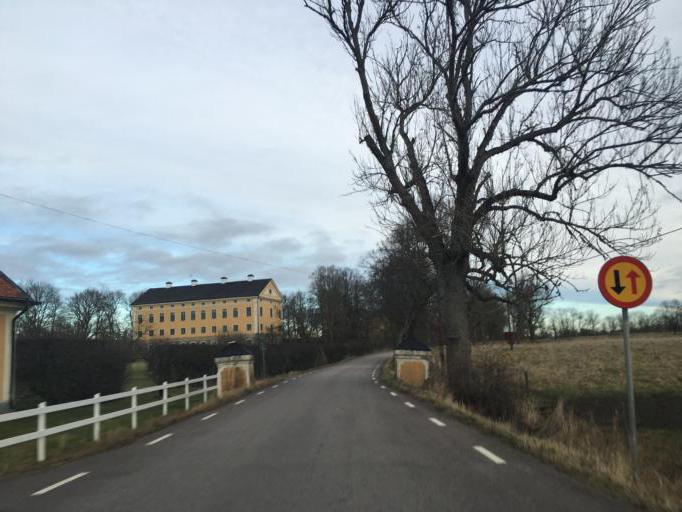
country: SE
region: OEstergoetland
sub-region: Norrkopings Kommun
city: Norrkoping
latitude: 58.4644
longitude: 16.1584
